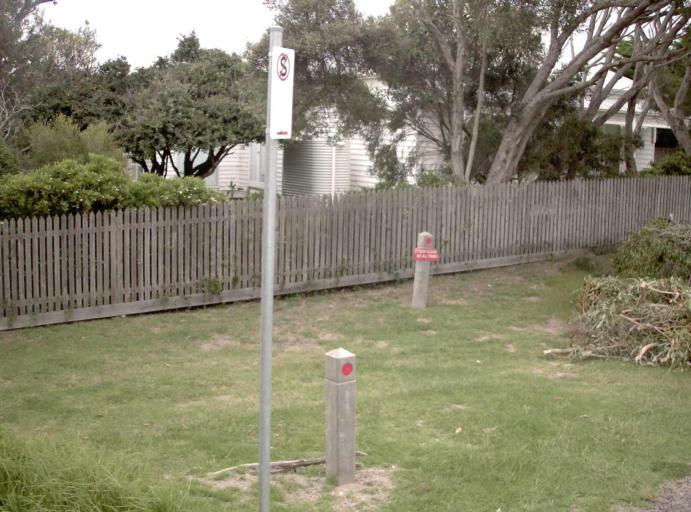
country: AU
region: Victoria
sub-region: Mornington Peninsula
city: Sorrento
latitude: -38.3190
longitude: 144.7047
